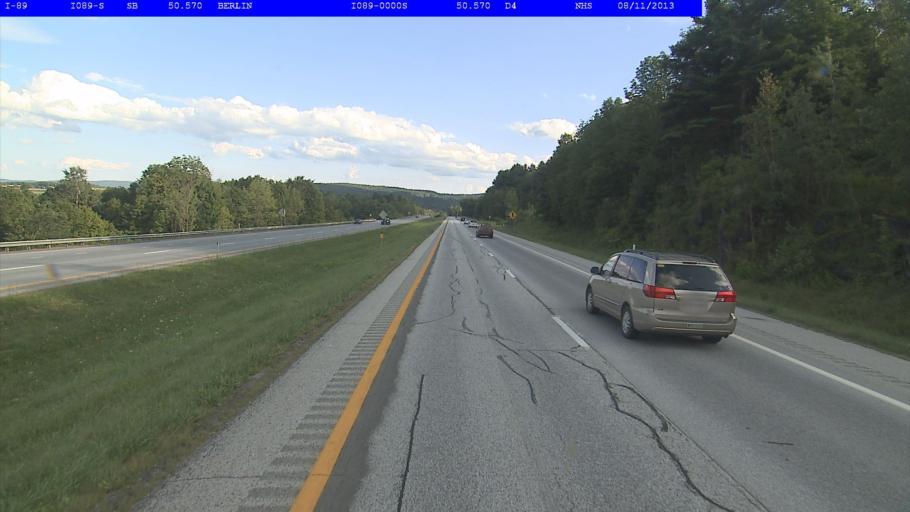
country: US
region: Vermont
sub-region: Washington County
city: Montpelier
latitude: 44.2196
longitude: -72.5847
